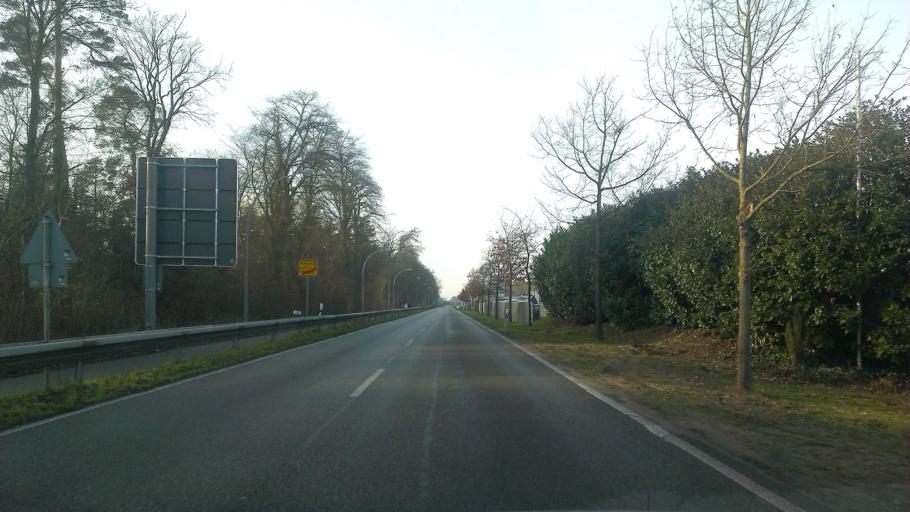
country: DE
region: Baden-Wuerttemberg
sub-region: Karlsruhe Region
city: Waghausel
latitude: 49.2467
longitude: 8.5321
